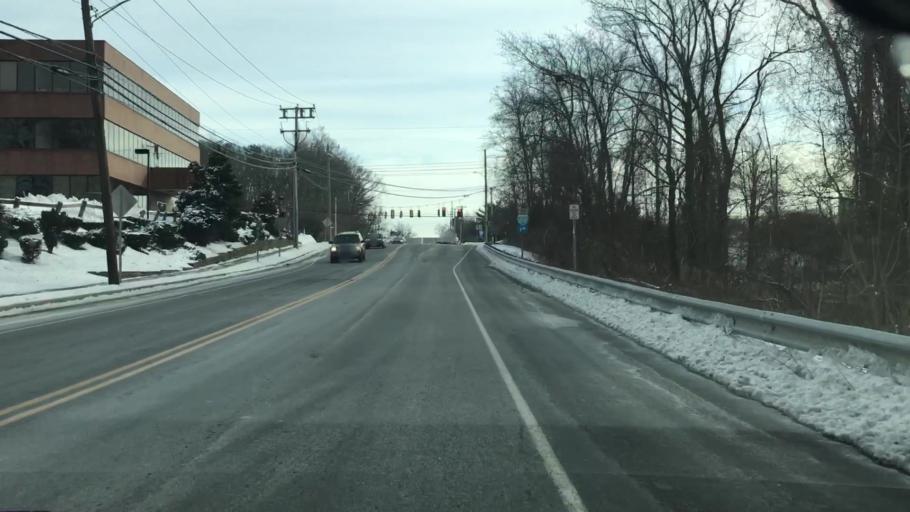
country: US
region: Connecticut
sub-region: Hartford County
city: East Hartford
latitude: 41.7708
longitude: -72.6194
